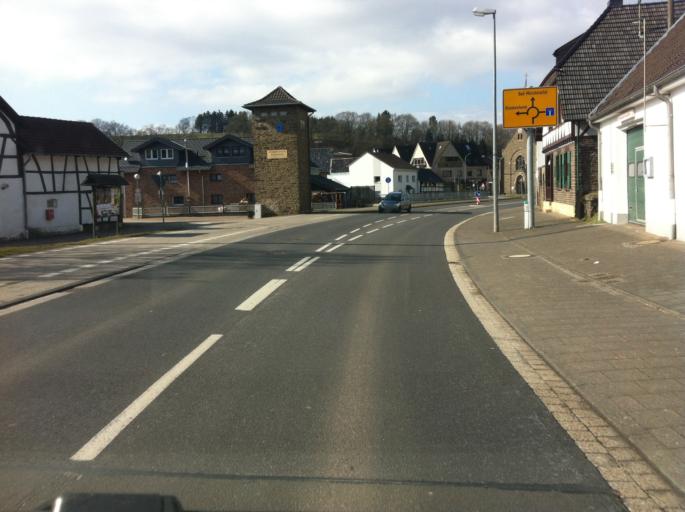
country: DE
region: North Rhine-Westphalia
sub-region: Regierungsbezirk Koln
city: Bad Munstereifel
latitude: 50.5327
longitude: 6.7709
